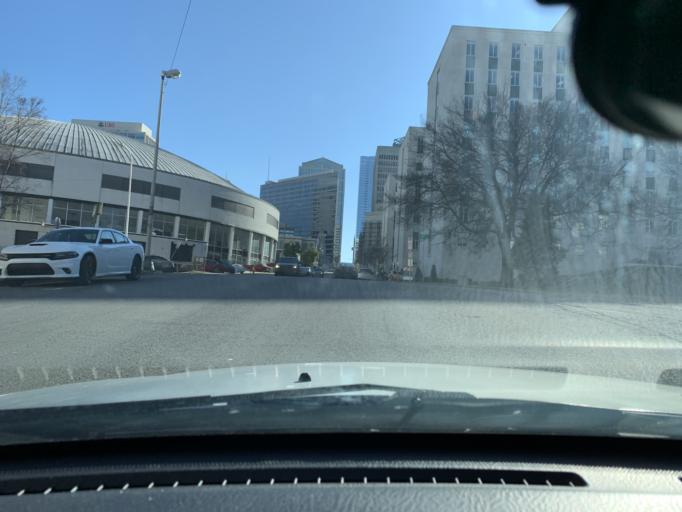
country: US
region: Tennessee
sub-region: Davidson County
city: Nashville
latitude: 36.1683
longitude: -86.7832
